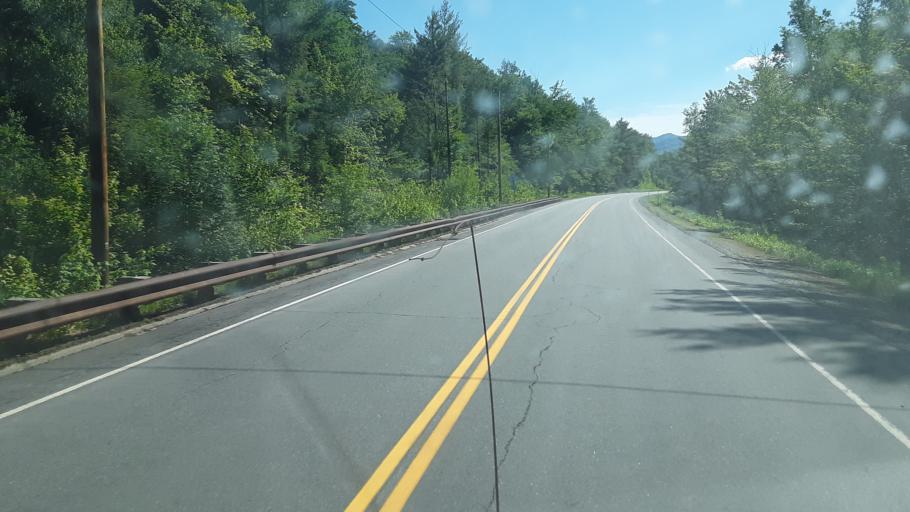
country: US
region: New Hampshire
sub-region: Grafton County
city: Woodstock
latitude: 44.0203
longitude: -71.7400
